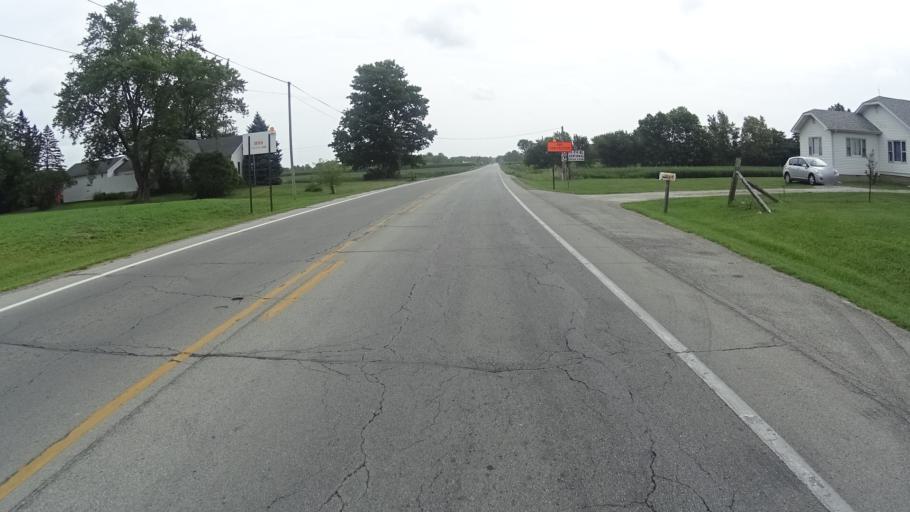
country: US
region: Indiana
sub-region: Madison County
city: Edgewood
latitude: 40.1021
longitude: -85.7860
